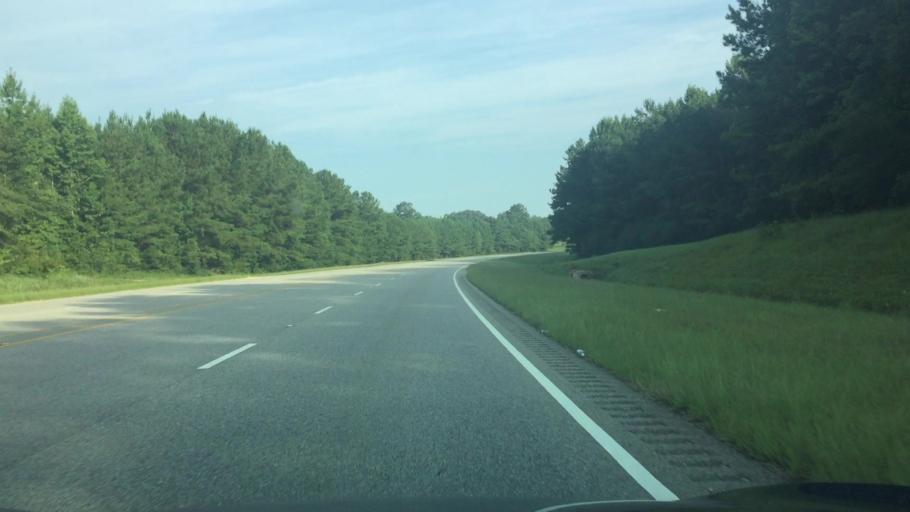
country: US
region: Alabama
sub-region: Butler County
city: Georgiana
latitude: 31.4680
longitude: -86.6634
